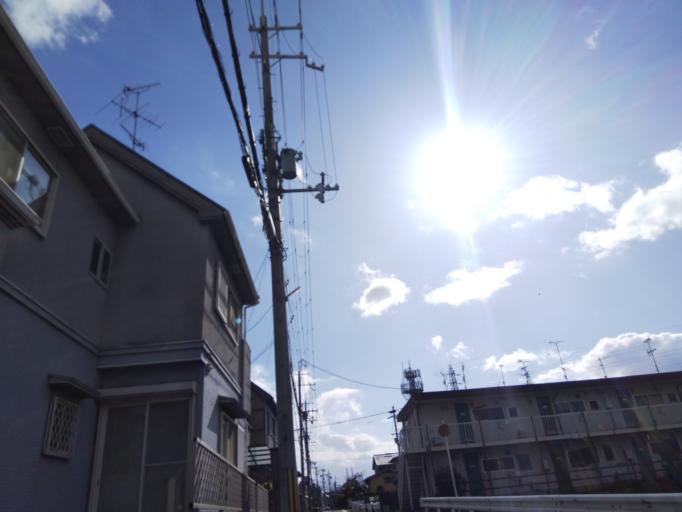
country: JP
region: Kyoto
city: Uji
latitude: 34.9287
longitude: 135.7970
